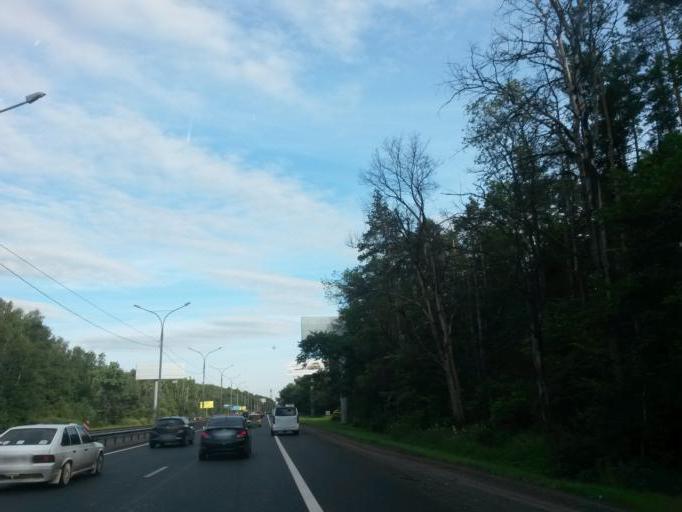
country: RU
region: Moskovskaya
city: Petrovskaya
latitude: 55.5425
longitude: 37.8010
